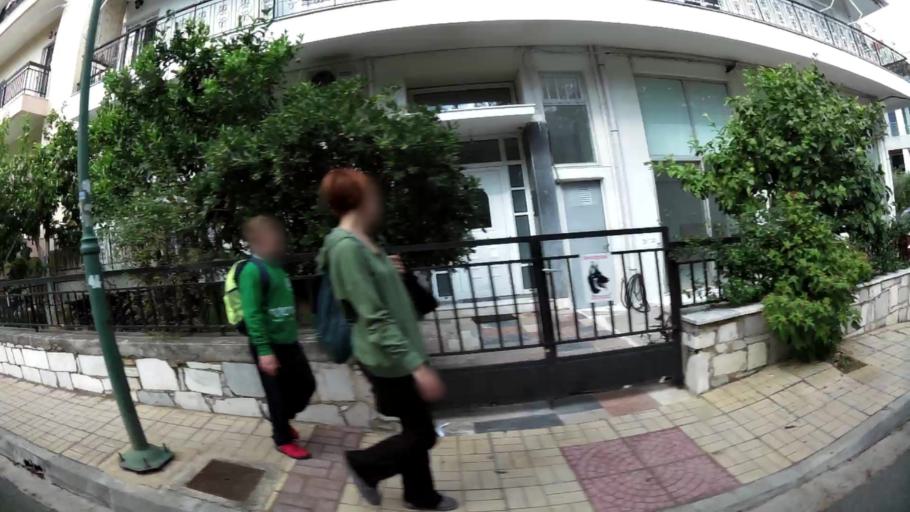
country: GR
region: Attica
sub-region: Nomarchia Athinas
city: Melissia
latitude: 38.0556
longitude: 23.8344
